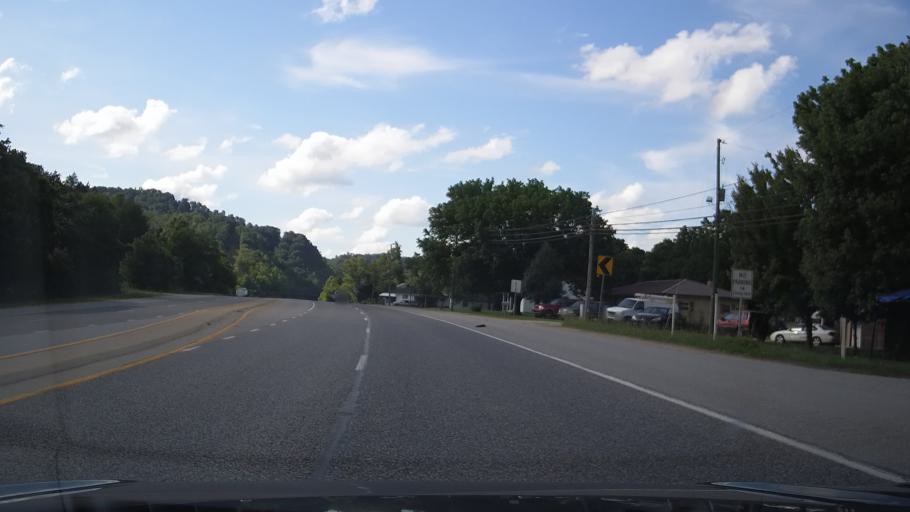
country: US
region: Kentucky
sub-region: Lawrence County
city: Louisa
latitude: 37.9949
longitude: -82.6584
